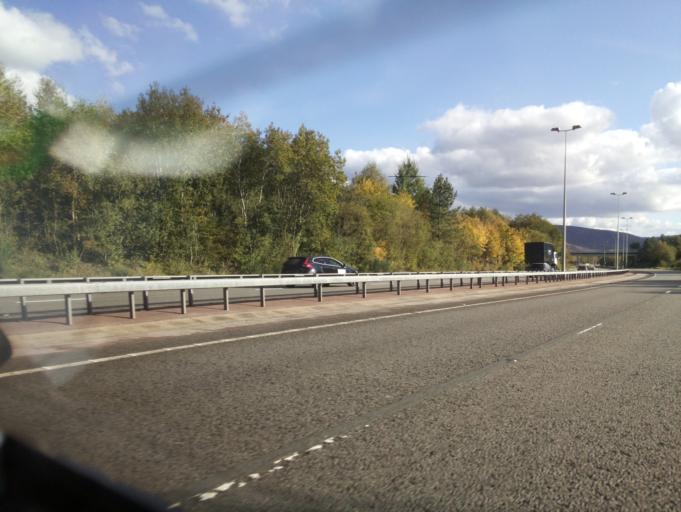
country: GB
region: Wales
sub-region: Merthyr Tydfil County Borough
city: Merthyr Tydfil
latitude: 51.7394
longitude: -3.3848
